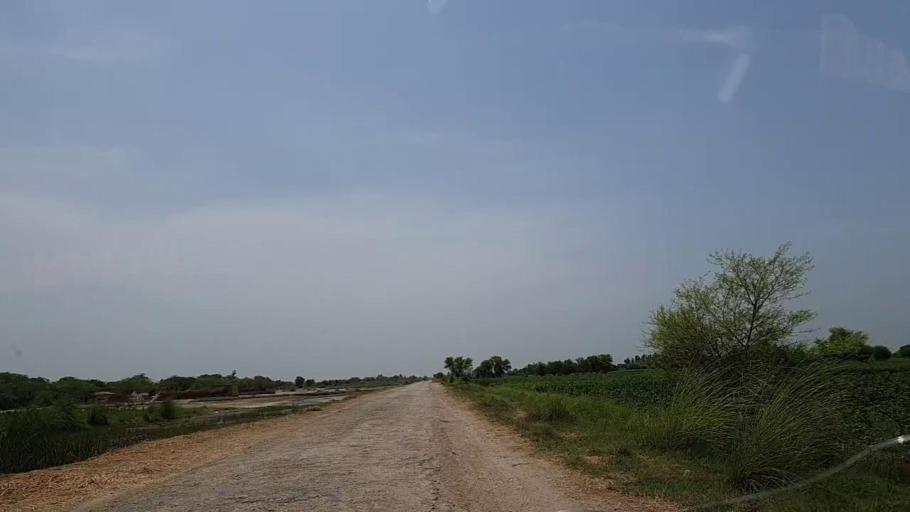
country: PK
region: Sindh
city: Khanpur
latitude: 27.8765
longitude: 69.4911
